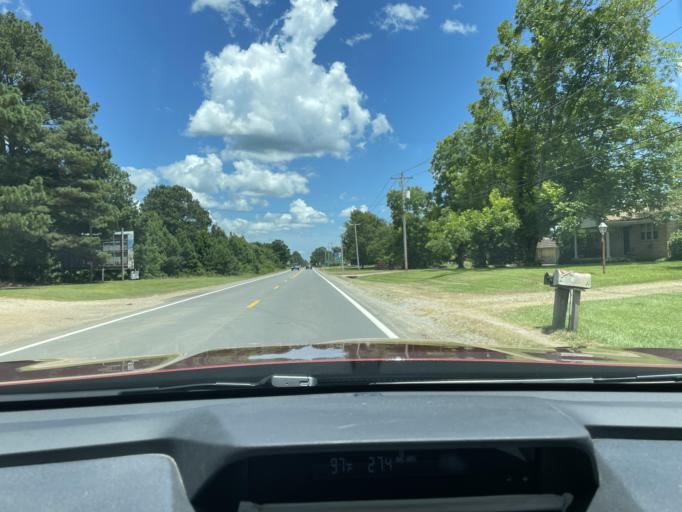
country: US
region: Arkansas
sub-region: Drew County
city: Monticello
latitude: 33.6286
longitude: -91.7626
